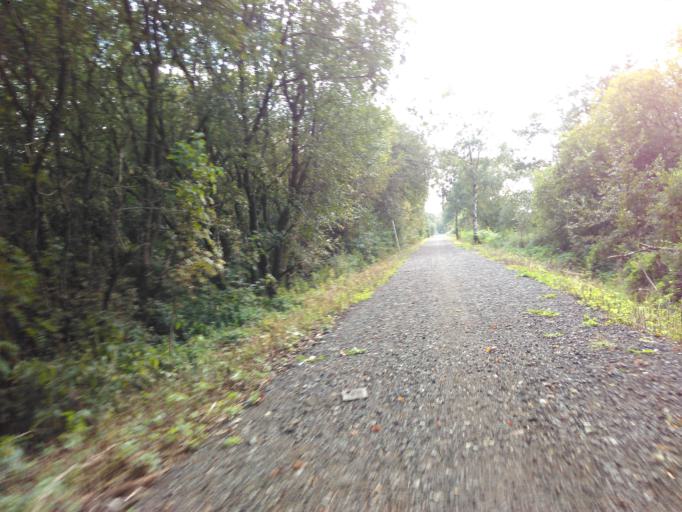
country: BE
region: Wallonia
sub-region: Province du Luxembourg
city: Neufchateau
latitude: 49.9107
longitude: 5.4440
